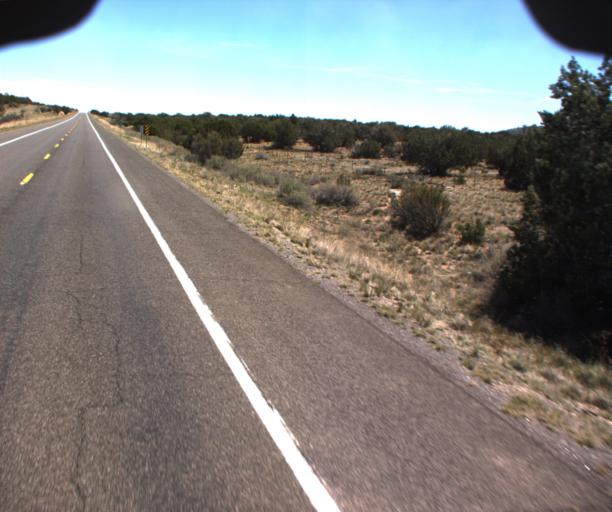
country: US
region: Arizona
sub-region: Mohave County
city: Peach Springs
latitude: 35.5502
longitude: -113.3058
